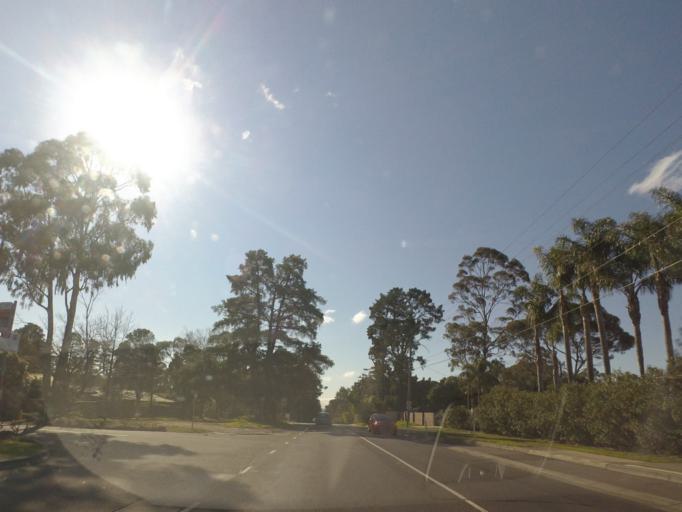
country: AU
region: Victoria
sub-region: Manningham
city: Donvale
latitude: -37.7952
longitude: 145.1795
